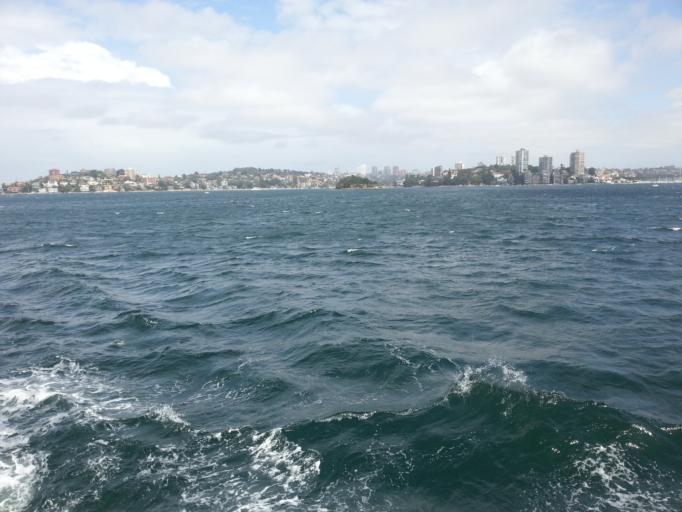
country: AU
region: New South Wales
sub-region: Mosman
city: Mosman
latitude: -33.8541
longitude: 151.2384
